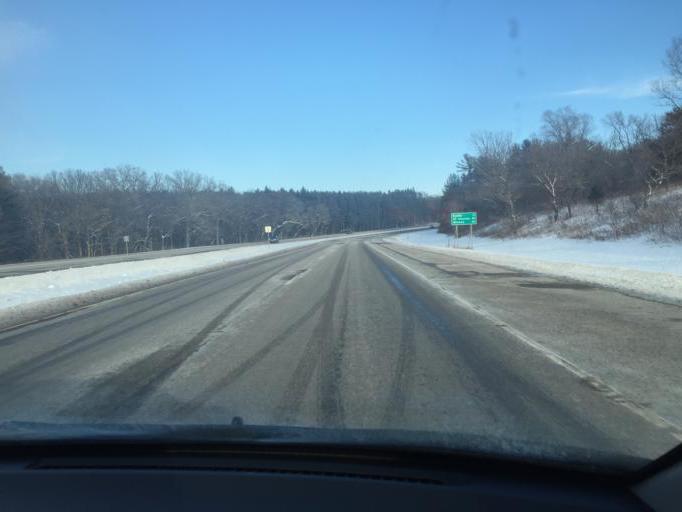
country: US
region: Minnesota
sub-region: Olmsted County
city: Rochester
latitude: 44.0113
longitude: -92.4317
